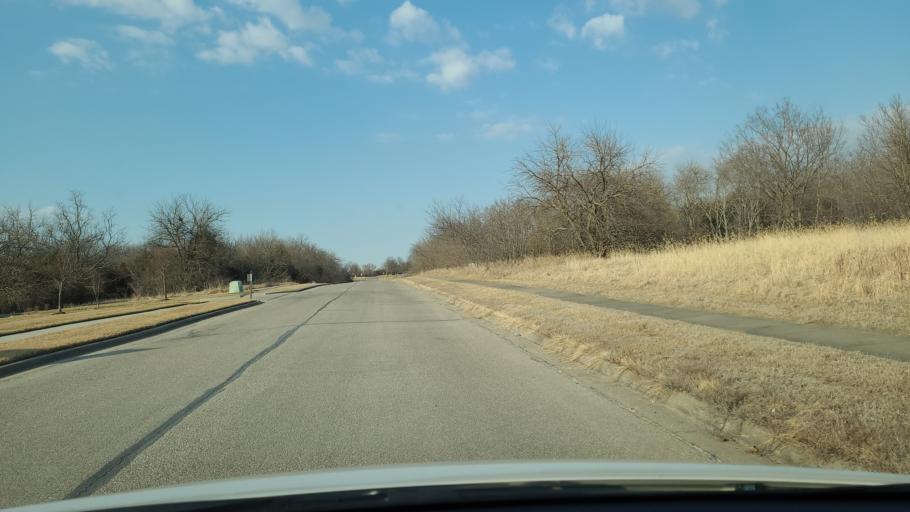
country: US
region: Kansas
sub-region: Douglas County
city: Lawrence
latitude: 38.9528
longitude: -95.3107
